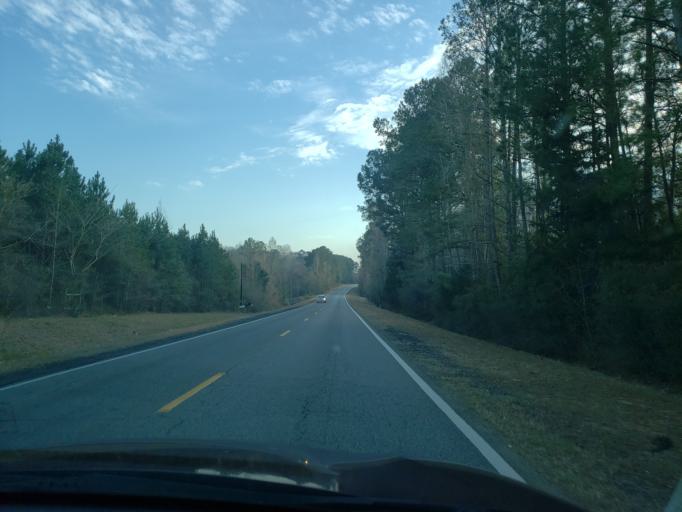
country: US
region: Alabama
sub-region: Hale County
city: Greensboro
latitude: 32.7387
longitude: -87.5857
